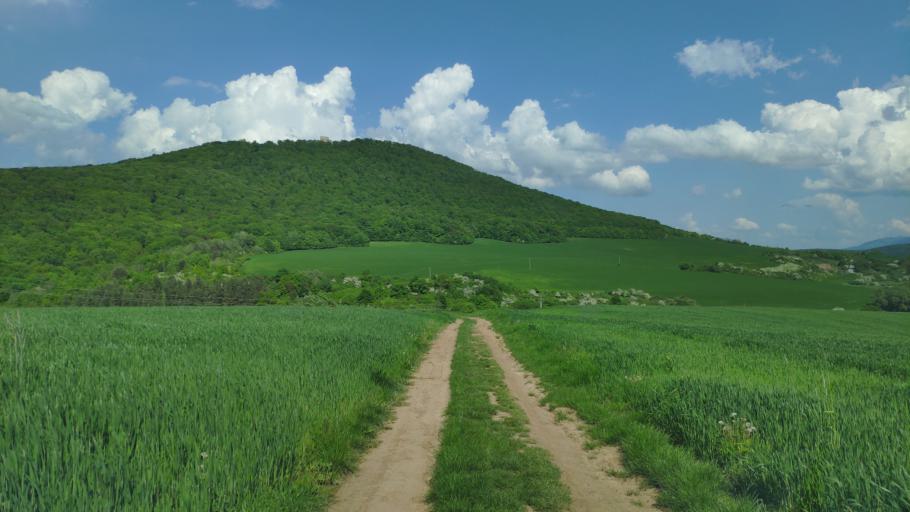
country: SK
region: Presovsky
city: Sabinov
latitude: 49.0463
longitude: 21.1592
